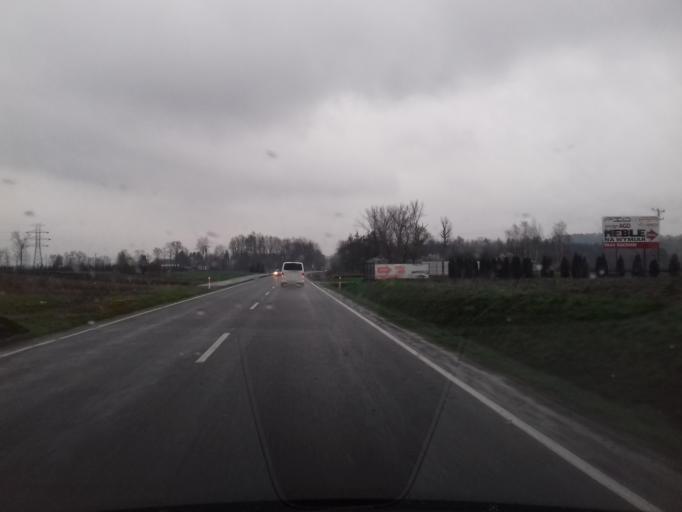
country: PL
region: Lesser Poland Voivodeship
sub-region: Powiat nowosadecki
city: Stary Sacz
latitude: 49.5568
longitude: 20.6549
